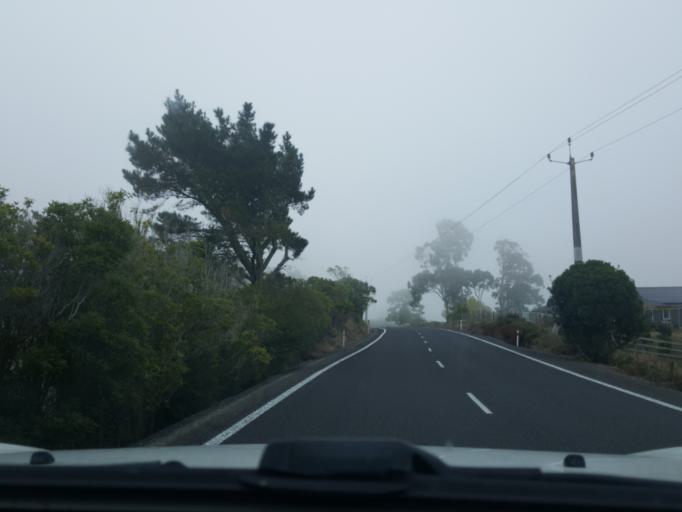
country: NZ
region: Auckland
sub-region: Auckland
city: Pukekohe East
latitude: -37.2974
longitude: 175.0336
